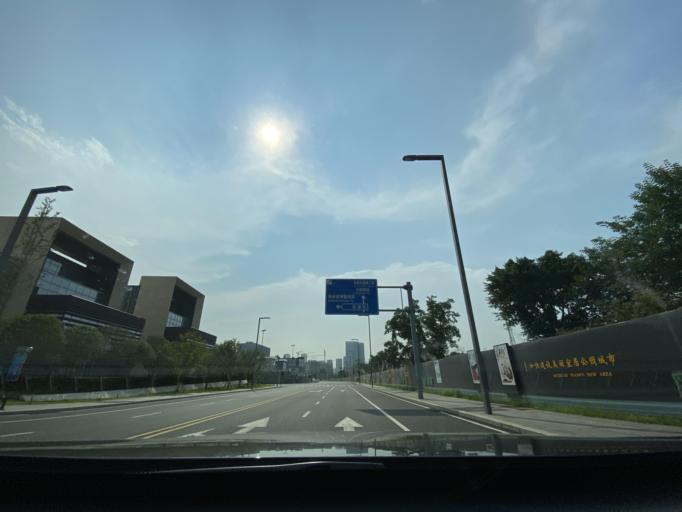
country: CN
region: Sichuan
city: Dongsheng
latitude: 30.3928
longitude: 104.0833
